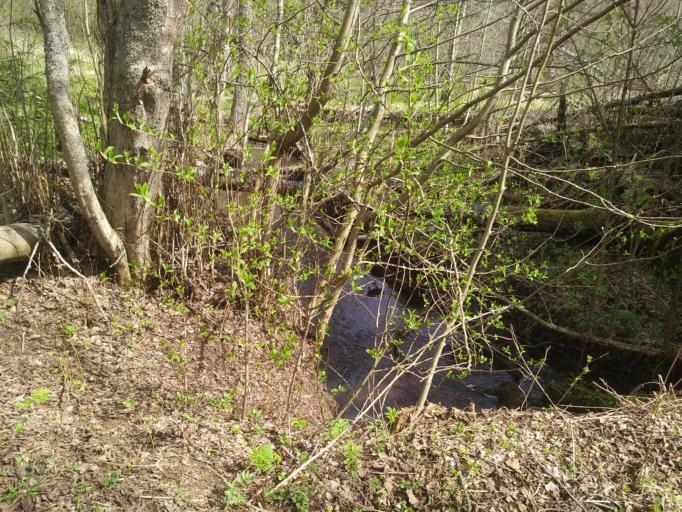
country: RU
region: Leningrad
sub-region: Vsevolzhskij Rajon
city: Vaskelovo
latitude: 60.5022
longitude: 30.4344
